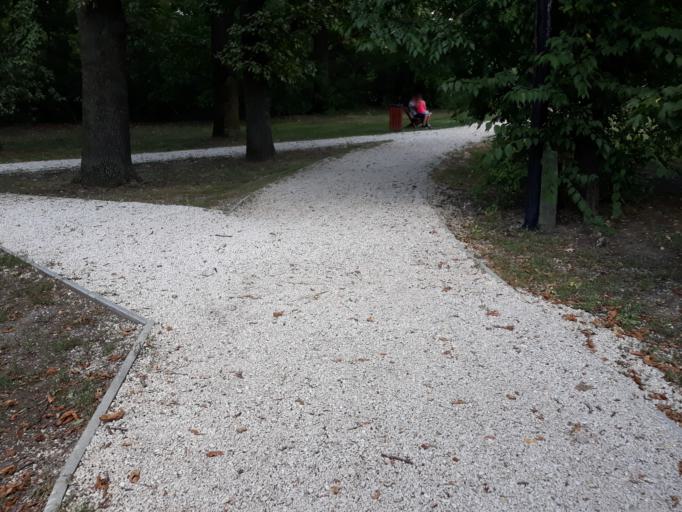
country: HU
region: Bekes
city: Oroshaza
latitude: 46.5678
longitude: 20.6245
